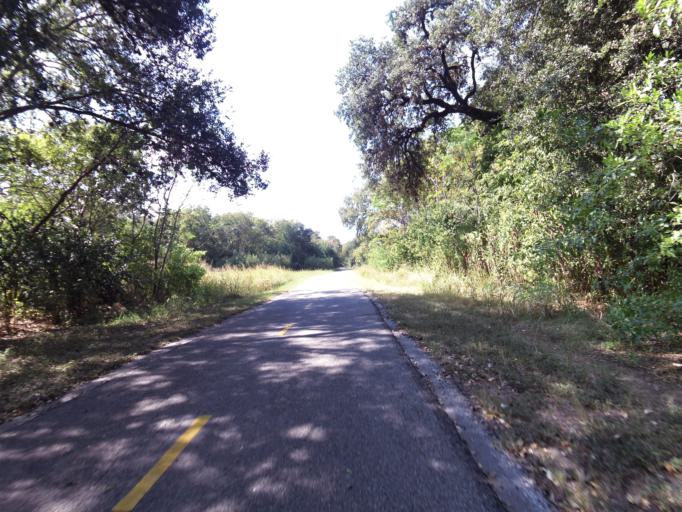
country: US
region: Texas
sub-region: Bexar County
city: Kirby
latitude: 29.4061
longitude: -98.4216
